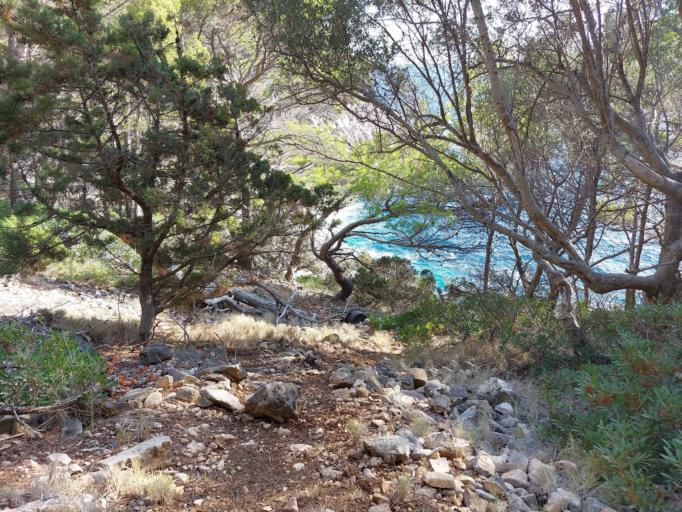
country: HR
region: Dubrovacko-Neretvanska
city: Smokvica
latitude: 42.7350
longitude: 16.8251
